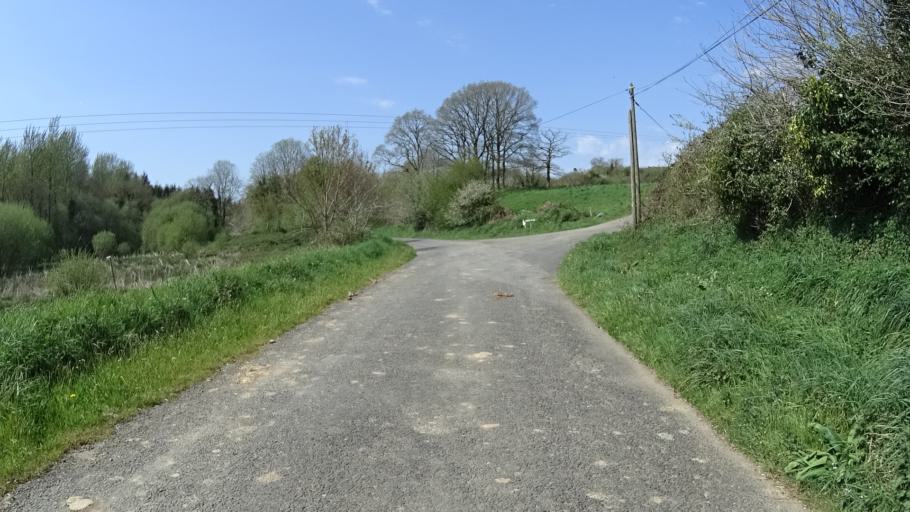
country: FR
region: Brittany
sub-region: Departement du Finistere
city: Sizun
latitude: 48.4151
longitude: -4.0913
